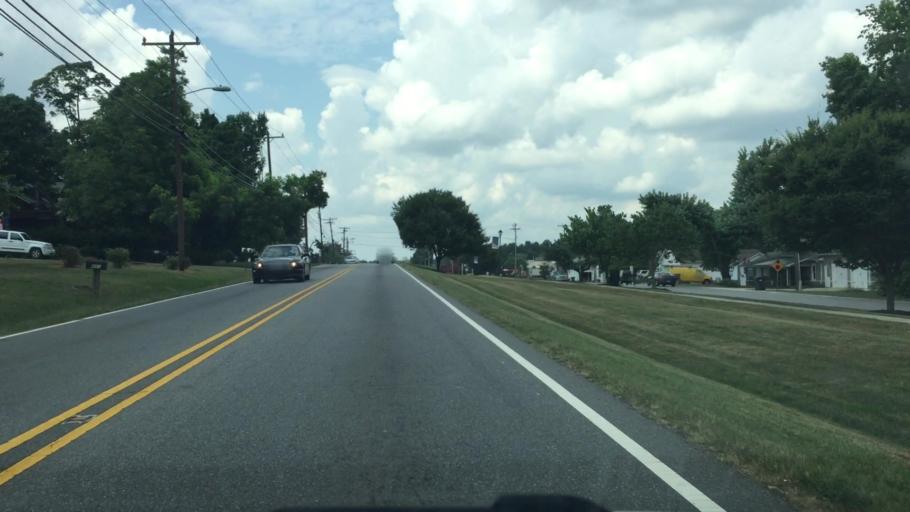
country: US
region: North Carolina
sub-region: Iredell County
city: Troutman
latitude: 35.7086
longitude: -80.8940
